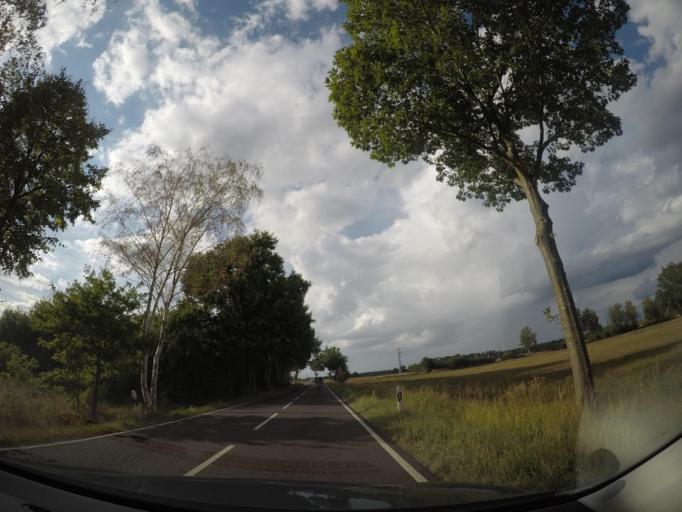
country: DE
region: Saxony-Anhalt
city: Mieste
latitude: 52.4828
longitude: 11.2543
